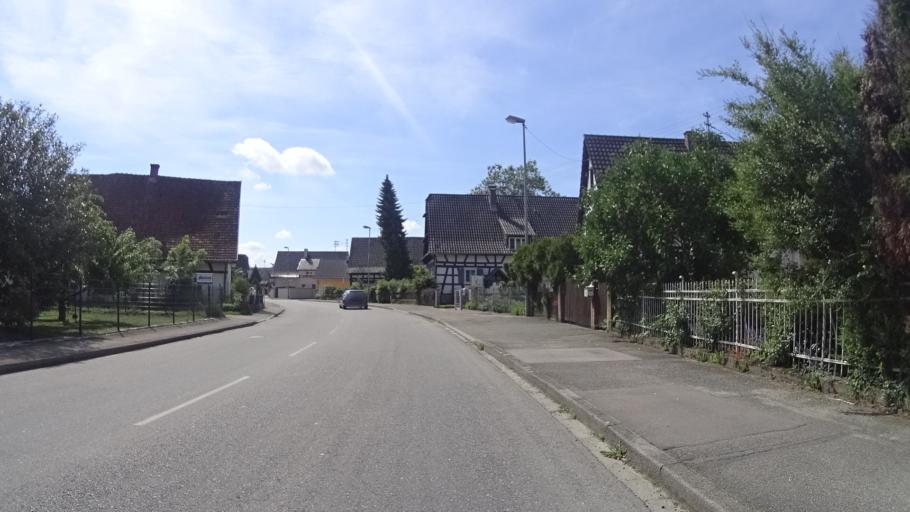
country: DE
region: Baden-Wuerttemberg
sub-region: Freiburg Region
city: Meissenheim
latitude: 48.4687
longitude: 7.8123
